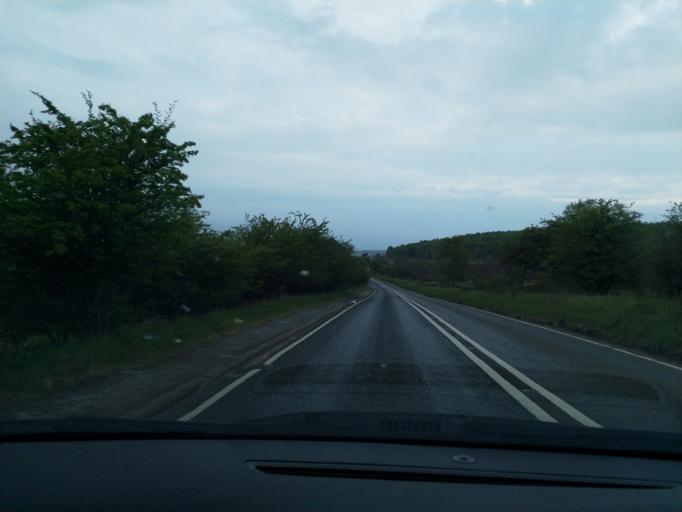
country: GB
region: England
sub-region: Derbyshire
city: Hathersage
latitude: 53.3218
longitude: -1.6111
